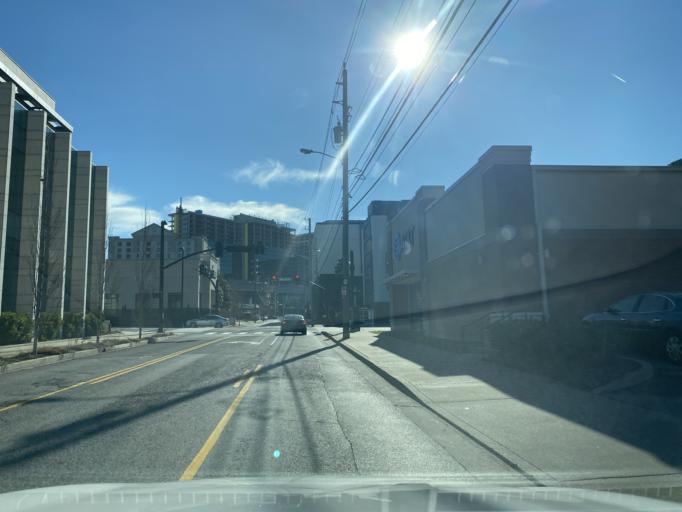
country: US
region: Tennessee
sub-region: Davidson County
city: Nashville
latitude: 36.1527
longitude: -86.7978
